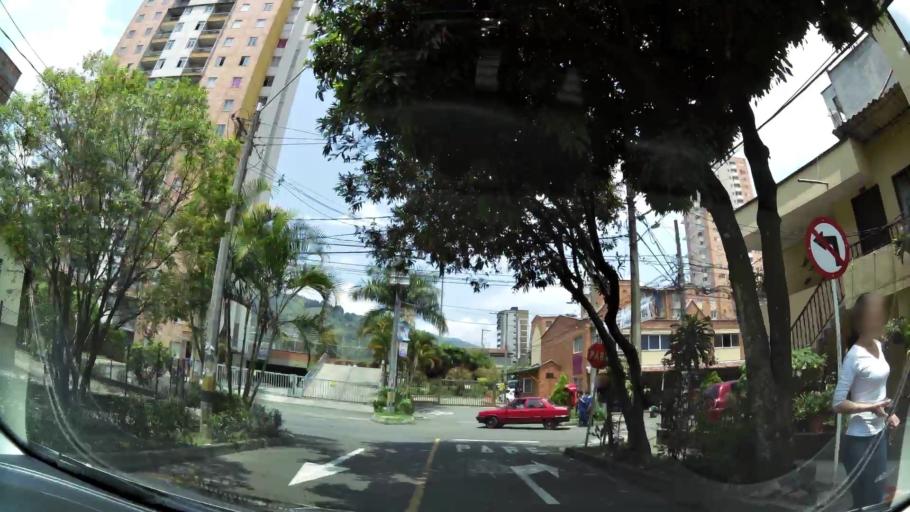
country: CO
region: Antioquia
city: Sabaneta
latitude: 6.1666
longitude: -75.6166
